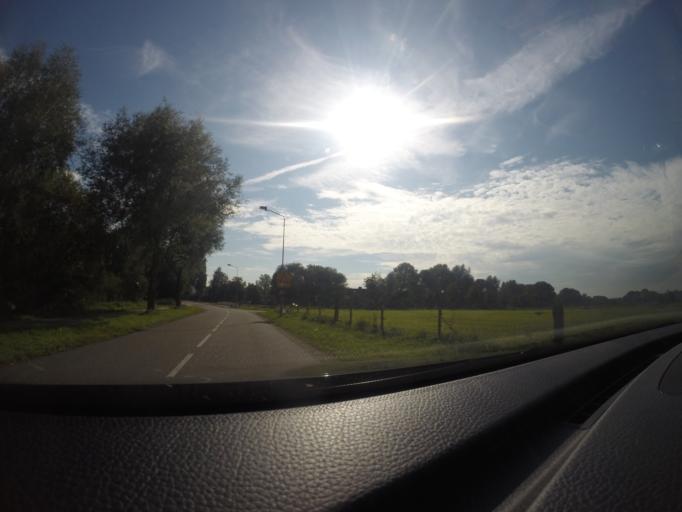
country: NL
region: Gelderland
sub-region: Gemeente Doetinchem
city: Doetinchem
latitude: 51.9423
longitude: 6.3471
